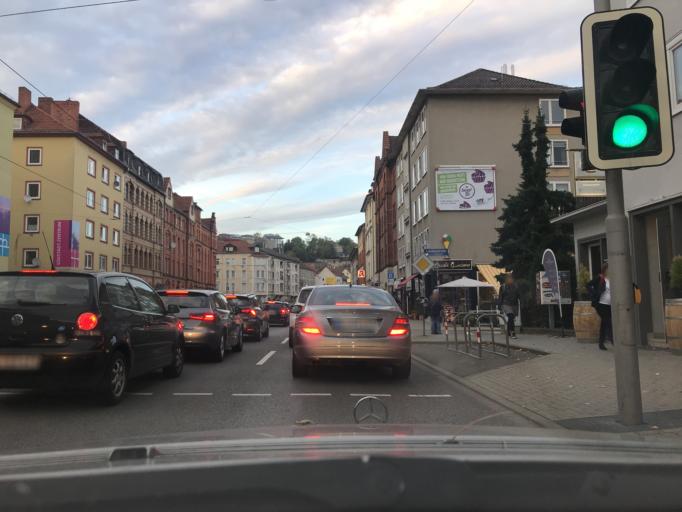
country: DE
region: Hesse
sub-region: Regierungsbezirk Kassel
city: Kassel
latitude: 51.3054
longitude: 9.4855
